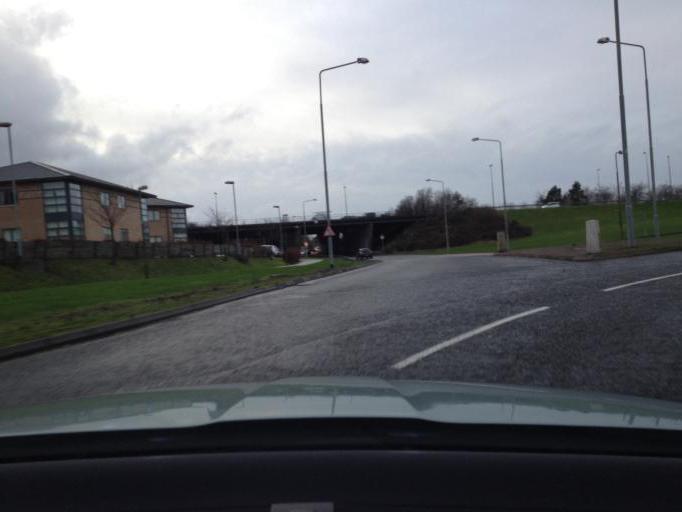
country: GB
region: Scotland
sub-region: West Lothian
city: Livingston
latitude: 55.9063
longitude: -3.5135
